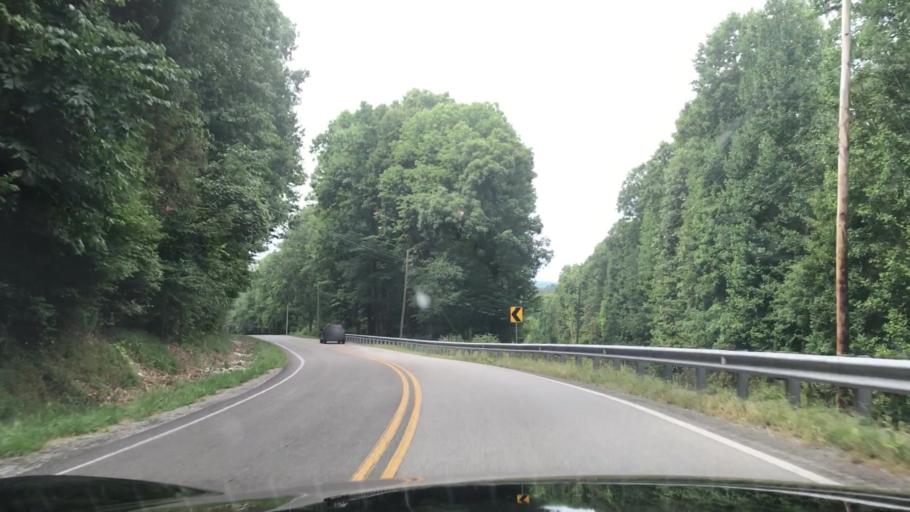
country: US
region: Kentucky
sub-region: Butler County
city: Morgantown
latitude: 37.2052
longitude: -86.7362
